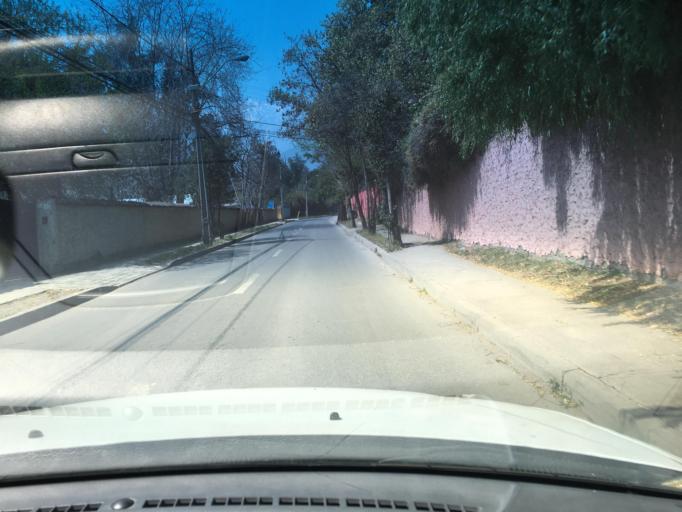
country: CL
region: Santiago Metropolitan
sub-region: Provincia de Santiago
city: Villa Presidente Frei, Nunoa, Santiago, Chile
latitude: -33.5140
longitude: -70.5462
